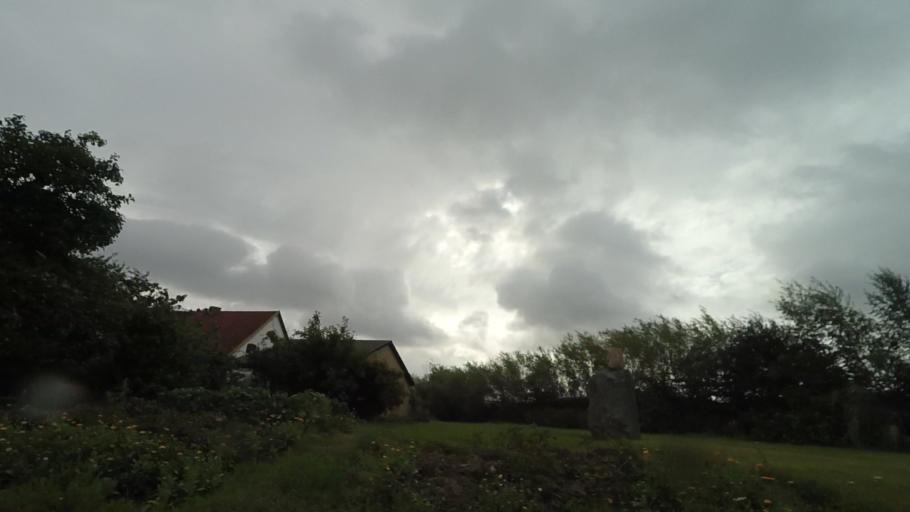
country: DK
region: Central Jutland
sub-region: Syddjurs Kommune
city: Ronde
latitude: 56.3124
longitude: 10.4613
